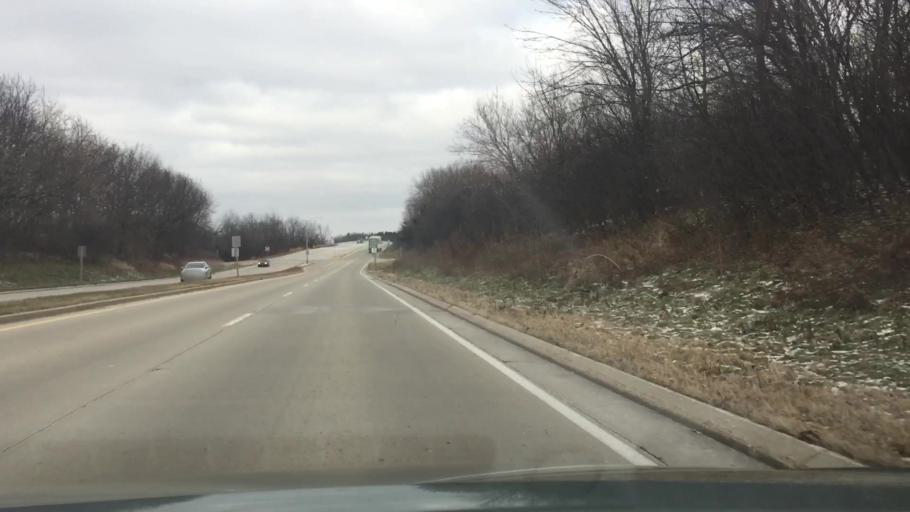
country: US
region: Wisconsin
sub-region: Waukesha County
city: Oconomowoc
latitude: 43.1026
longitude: -88.4804
